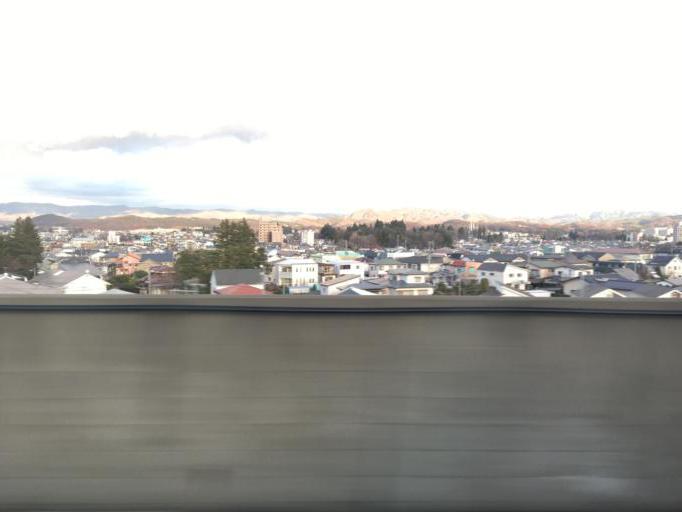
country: JP
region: Iwate
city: Morioka-shi
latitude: 39.7198
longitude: 141.1177
